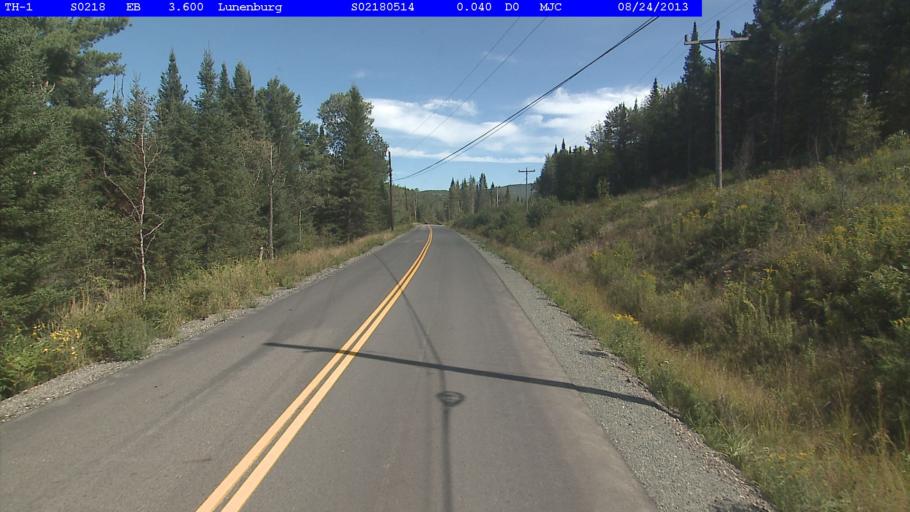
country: US
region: New Hampshire
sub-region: Grafton County
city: Littleton
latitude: 44.4206
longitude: -71.7467
